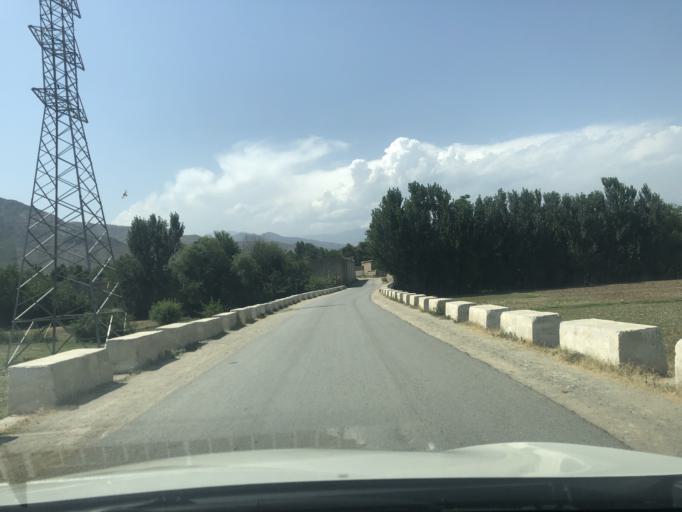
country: PK
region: Khyber Pakhtunkhwa
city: Timurgara
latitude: 34.7947
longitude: 71.6619
